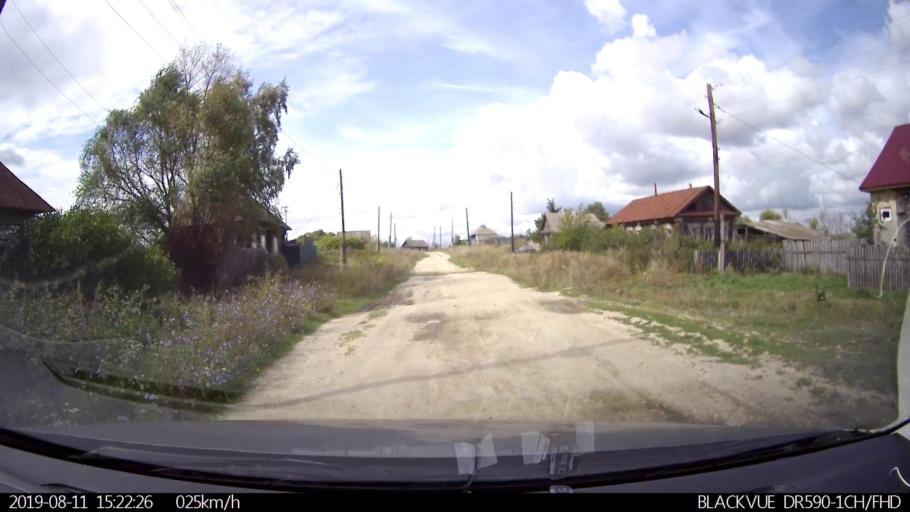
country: RU
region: Ulyanovsk
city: Ignatovka
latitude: 53.8464
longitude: 47.5813
